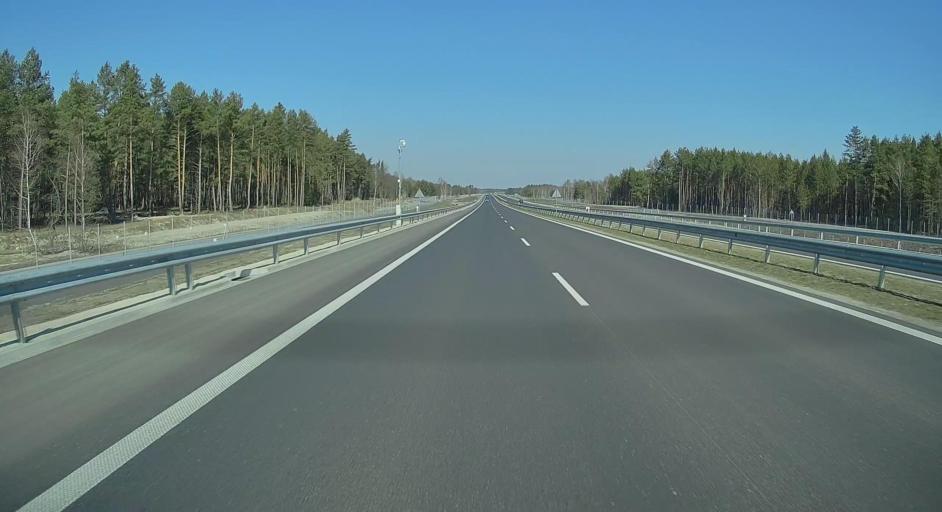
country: PL
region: Subcarpathian Voivodeship
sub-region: Powiat nizanski
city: Konczyce
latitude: 50.4420
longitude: 22.1402
